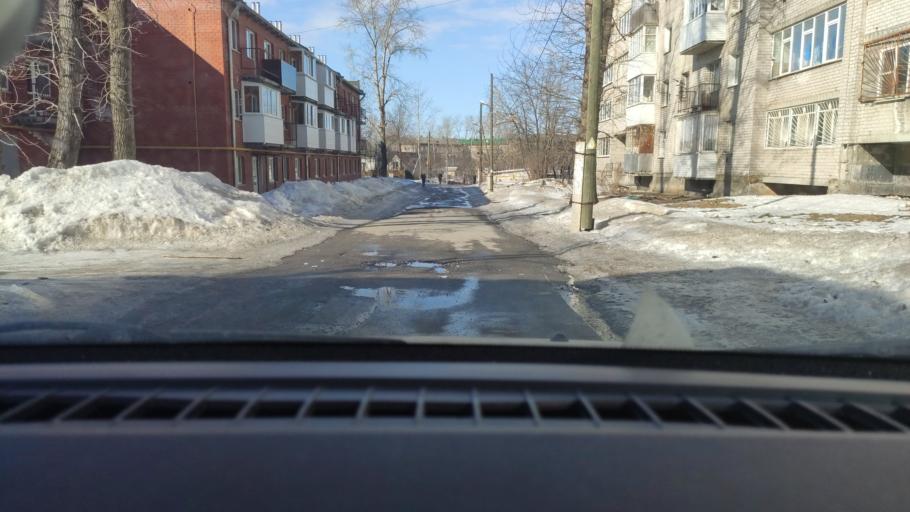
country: RU
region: Perm
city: Polazna
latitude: 58.1274
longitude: 56.3845
